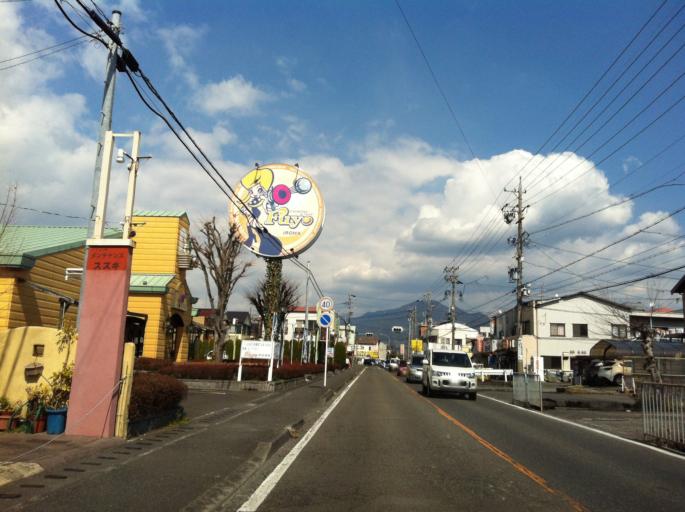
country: JP
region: Shizuoka
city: Shizuoka-shi
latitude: 35.0018
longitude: 138.3642
